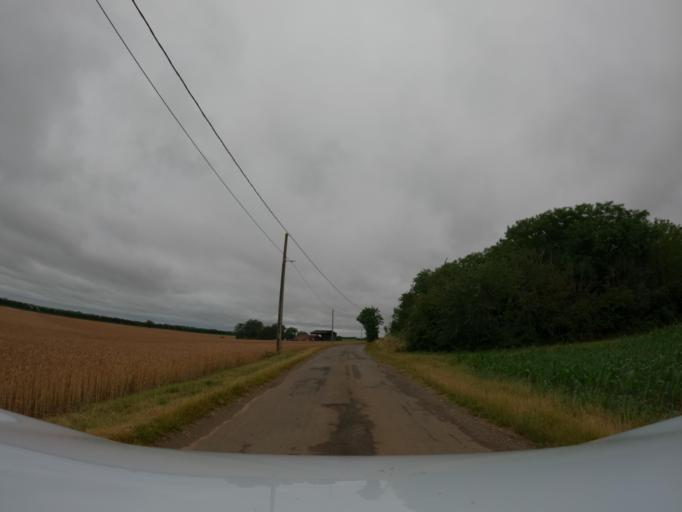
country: FR
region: Pays de la Loire
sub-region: Departement de la Vendee
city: Maillezais
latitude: 46.4181
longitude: -0.7163
